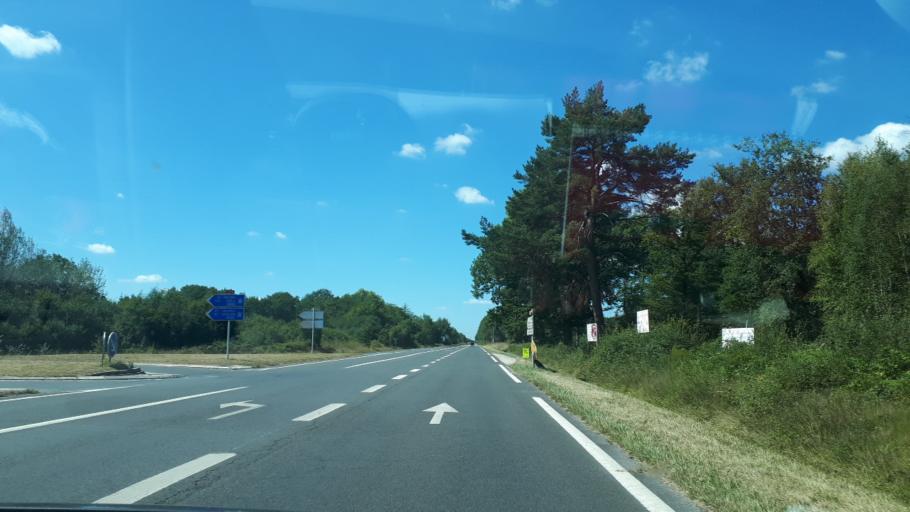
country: FR
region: Centre
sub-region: Departement du Loir-et-Cher
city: Lamotte-Beuvron
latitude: 47.5834
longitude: 1.9873
